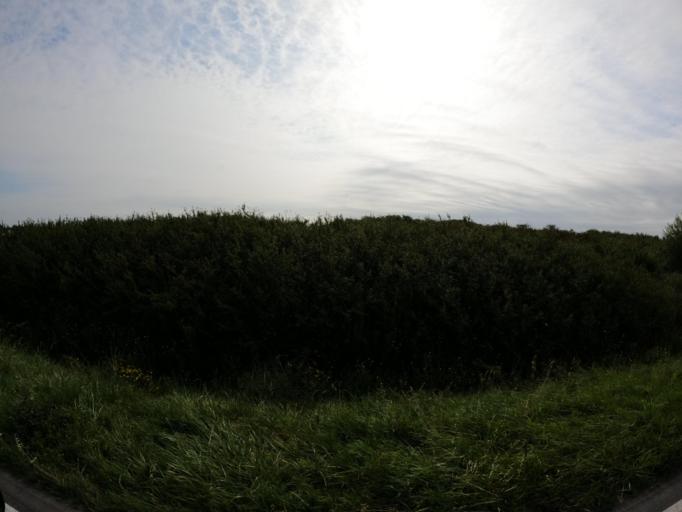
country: FR
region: Pays de la Loire
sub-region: Departement de la Vendee
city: Triaize
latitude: 46.3752
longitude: -1.2036
